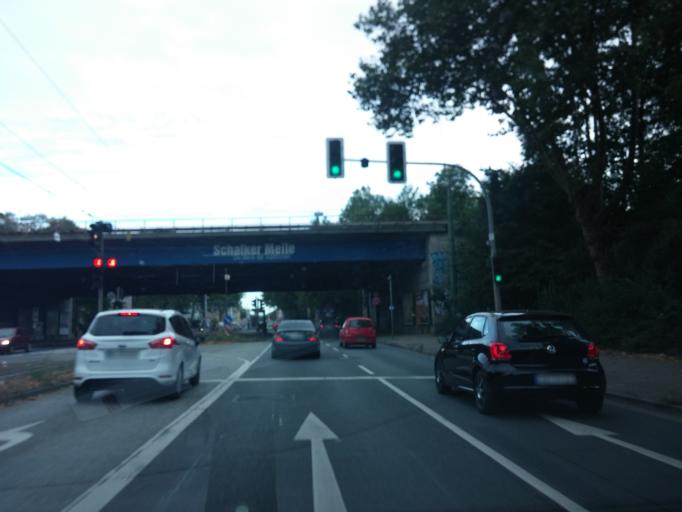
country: DE
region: North Rhine-Westphalia
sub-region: Regierungsbezirk Munster
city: Gelsenkirchen
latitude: 51.5320
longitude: 7.0795
